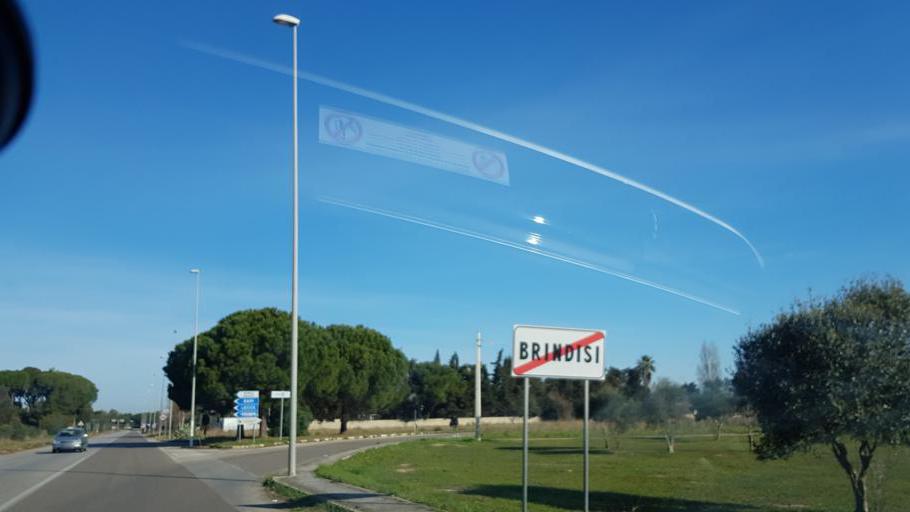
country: IT
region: Apulia
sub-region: Provincia di Brindisi
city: Brindisi
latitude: 40.6530
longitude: 17.9322
